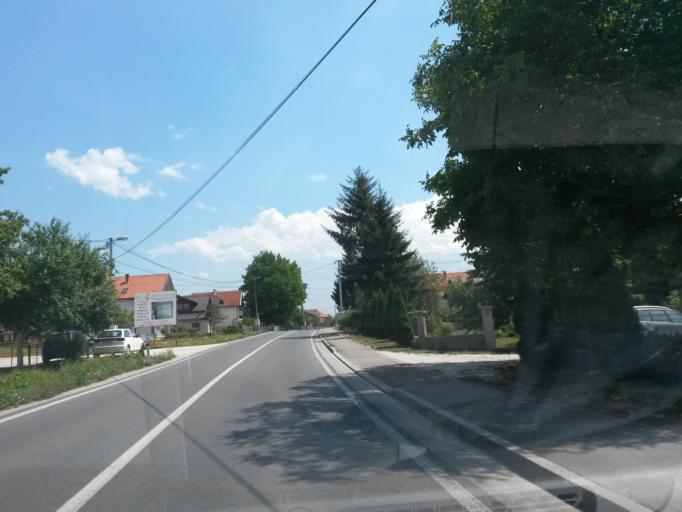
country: BA
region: Federation of Bosnia and Herzegovina
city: Travnik
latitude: 44.2130
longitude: 17.7054
